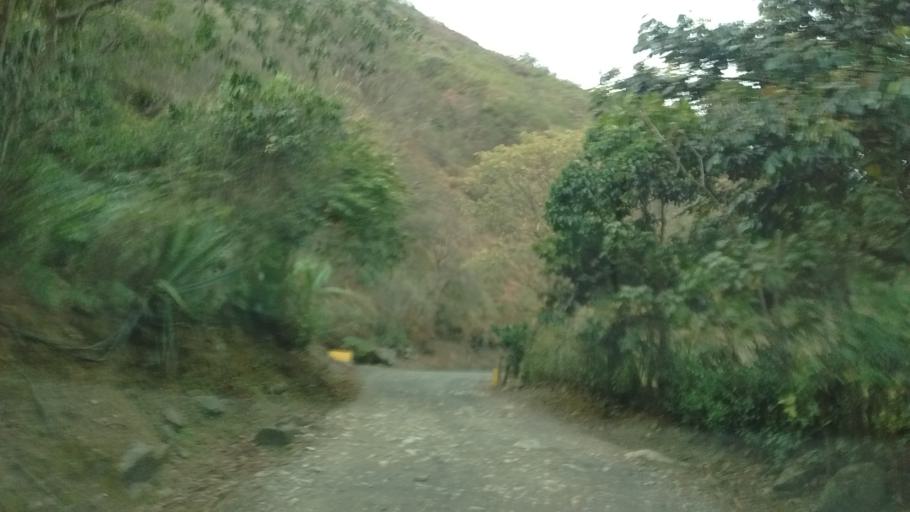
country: CO
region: Cauca
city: Almaguer
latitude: 1.8432
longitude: -76.9152
